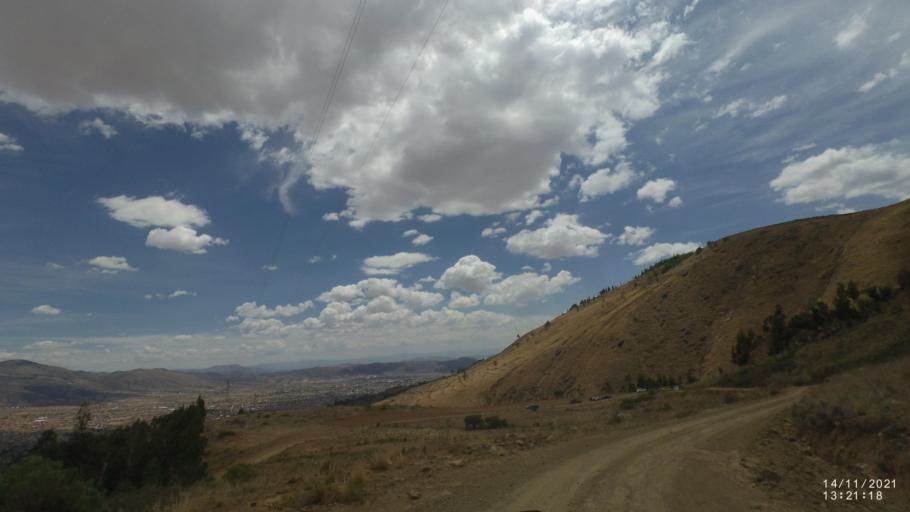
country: BO
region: Cochabamba
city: Colomi
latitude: -17.3755
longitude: -65.9822
